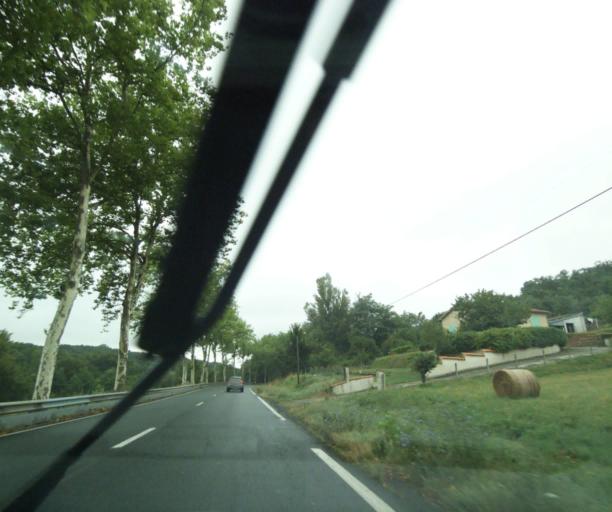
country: FR
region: Midi-Pyrenees
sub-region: Departement du Tarn
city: Le Garric
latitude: 43.9822
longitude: 2.1738
